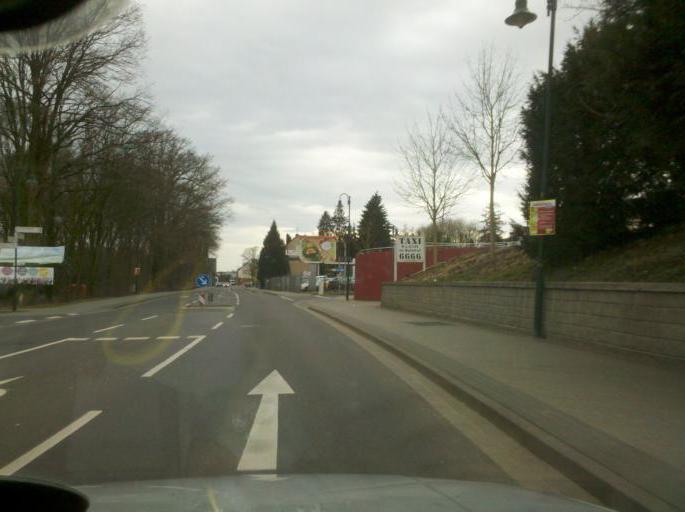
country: DE
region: North Rhine-Westphalia
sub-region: Regierungsbezirk Koln
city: Rosrath
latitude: 50.9015
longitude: 7.1832
